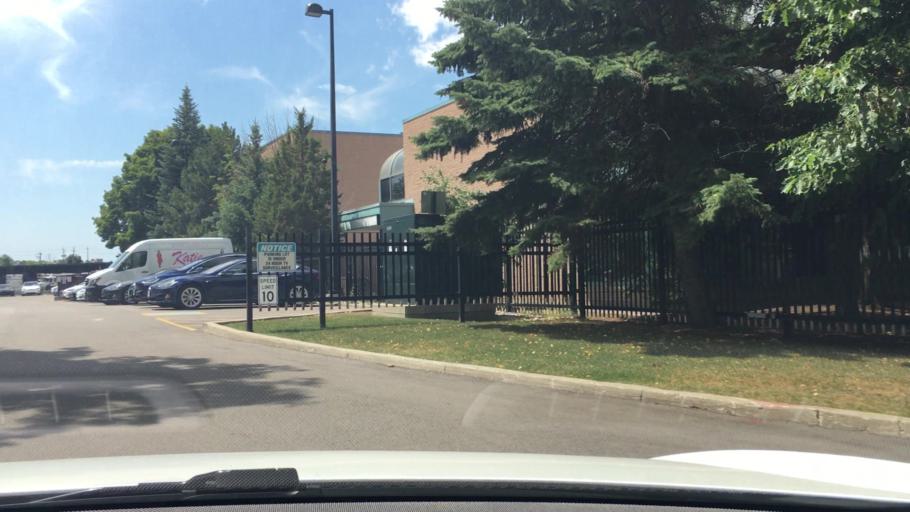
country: CA
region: Ontario
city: Scarborough
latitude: 43.7409
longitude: -79.3224
